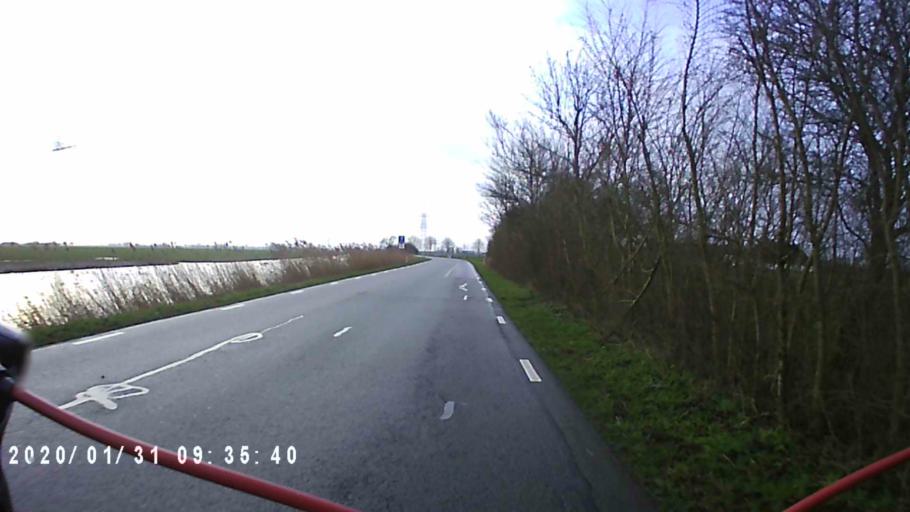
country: NL
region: Groningen
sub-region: Gemeente Winsum
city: Winsum
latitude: 53.3023
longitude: 6.4808
